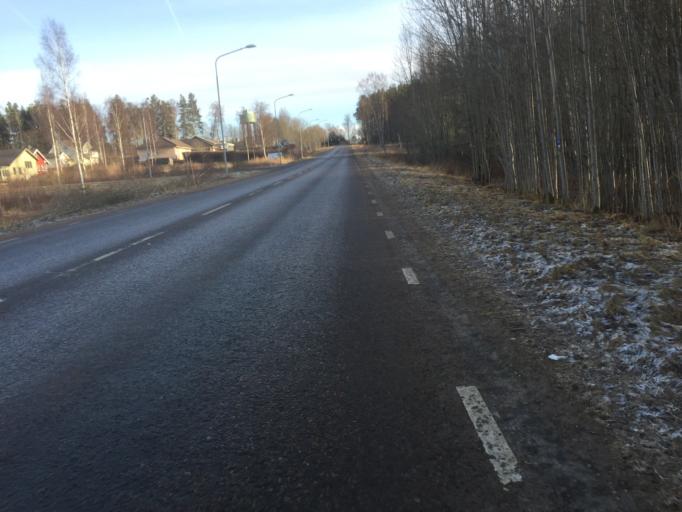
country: SE
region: Joenkoeping
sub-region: Aneby Kommun
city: Aneby
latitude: 57.8382
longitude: 14.7958
